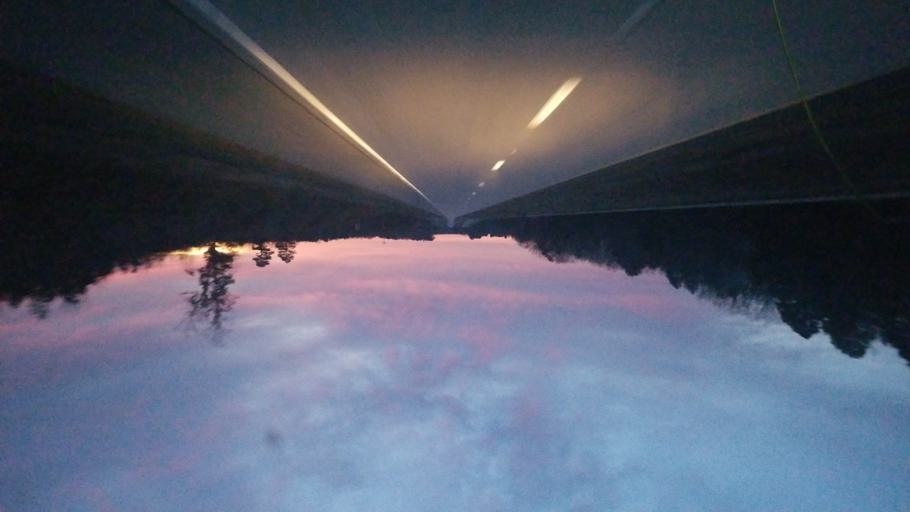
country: US
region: Missouri
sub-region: Shannon County
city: Winona
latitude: 36.9976
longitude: -91.4427
